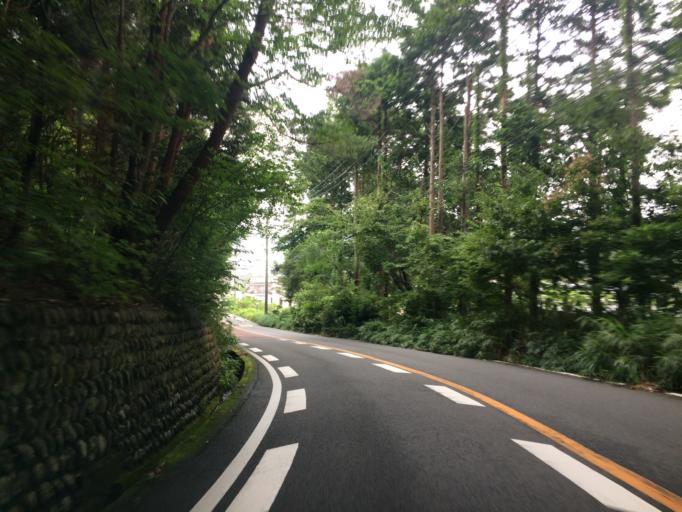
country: JP
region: Shizuoka
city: Shimada
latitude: 34.7988
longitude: 138.2023
